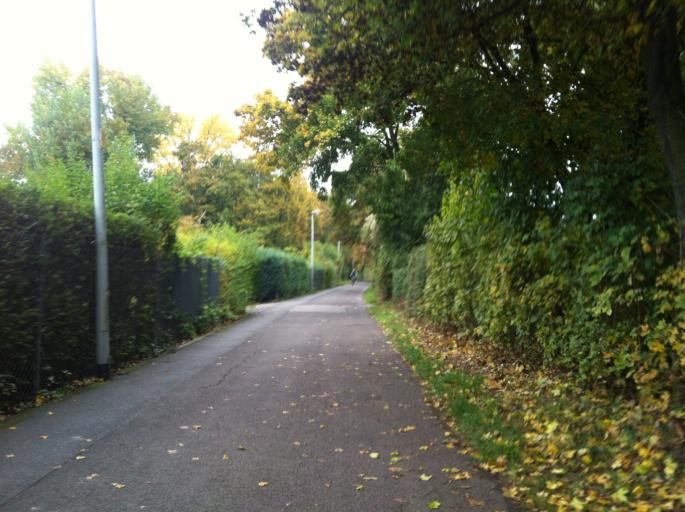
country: DE
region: Rheinland-Pfalz
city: Mainz
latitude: 49.9826
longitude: 8.2874
